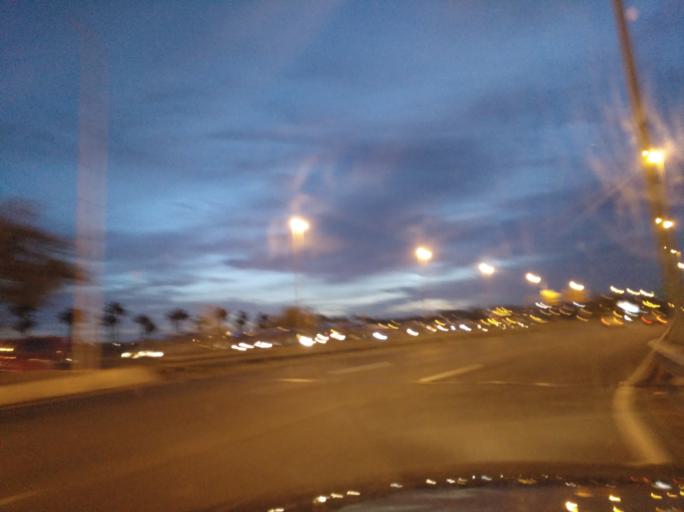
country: ES
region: Andalusia
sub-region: Provincia de Sevilla
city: Camas
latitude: 37.3896
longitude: -6.0144
